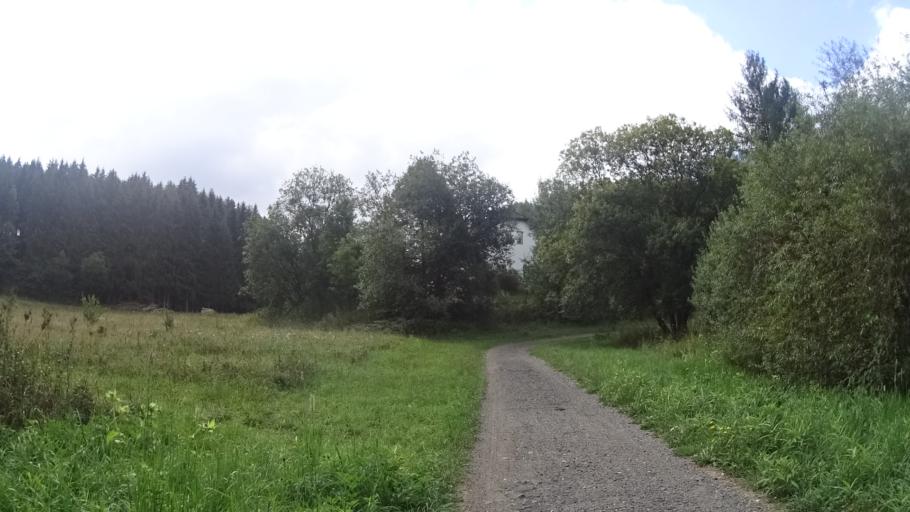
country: CZ
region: Pardubicky
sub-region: Okres Usti nad Orlici
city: Lanskroun
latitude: 49.9213
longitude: 16.5649
